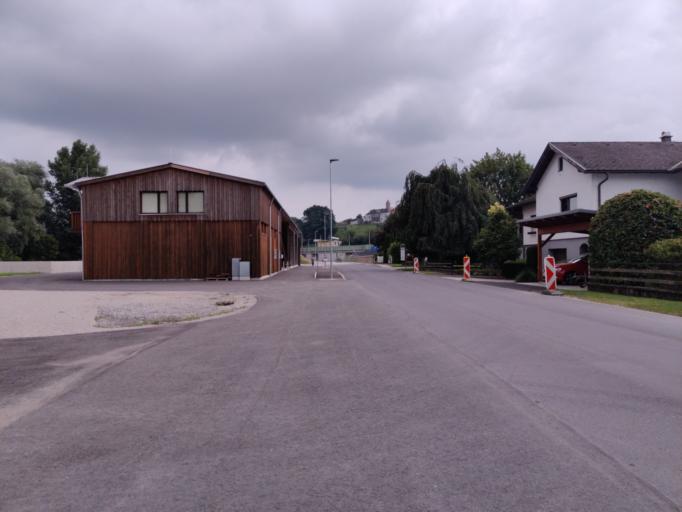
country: AT
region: Lower Austria
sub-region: Politischer Bezirk Melk
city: Ybbs an der Donau
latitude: 48.1698
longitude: 15.1116
